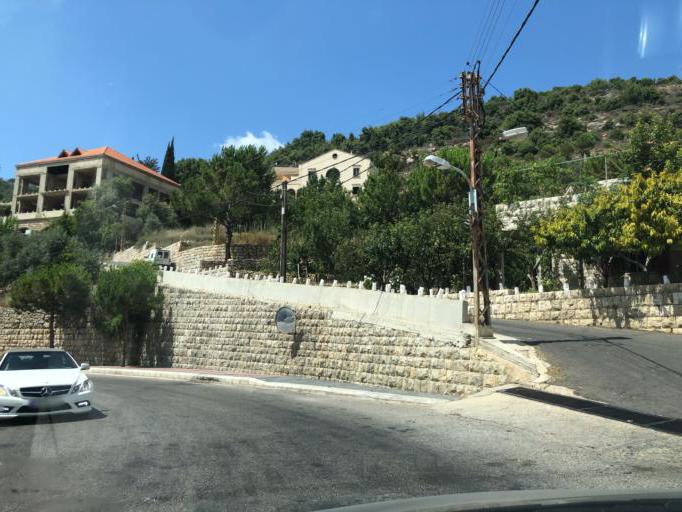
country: LB
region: Mont-Liban
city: Beit ed Dine
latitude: 33.7000
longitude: 35.5992
